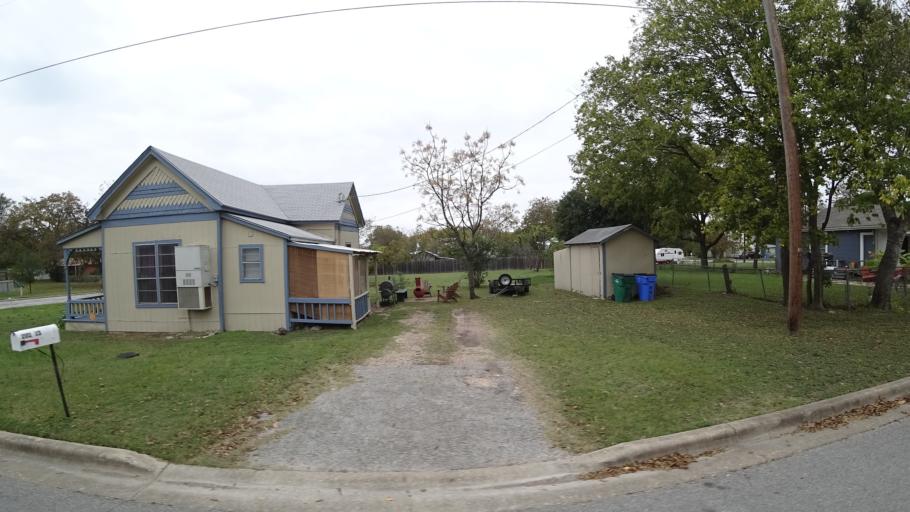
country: US
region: Texas
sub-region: Travis County
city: Pflugerville
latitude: 30.4390
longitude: -97.6234
